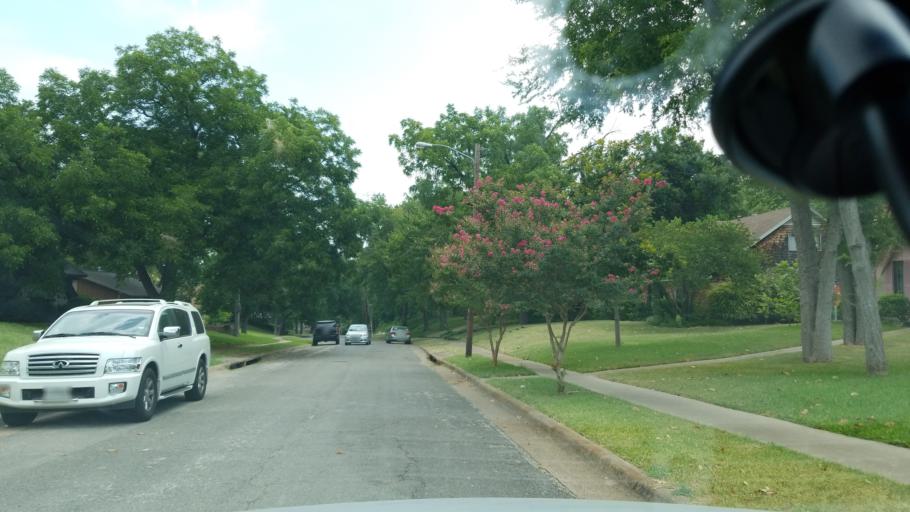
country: US
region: Texas
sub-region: Dallas County
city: Cockrell Hill
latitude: 32.6929
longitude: -96.8497
